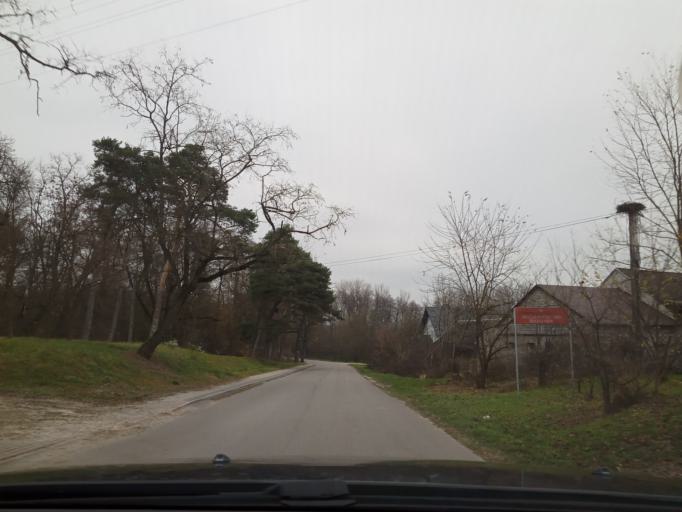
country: PL
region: Swietokrzyskie
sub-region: Powiat jedrzejowski
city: Imielno
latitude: 50.5858
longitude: 20.4740
